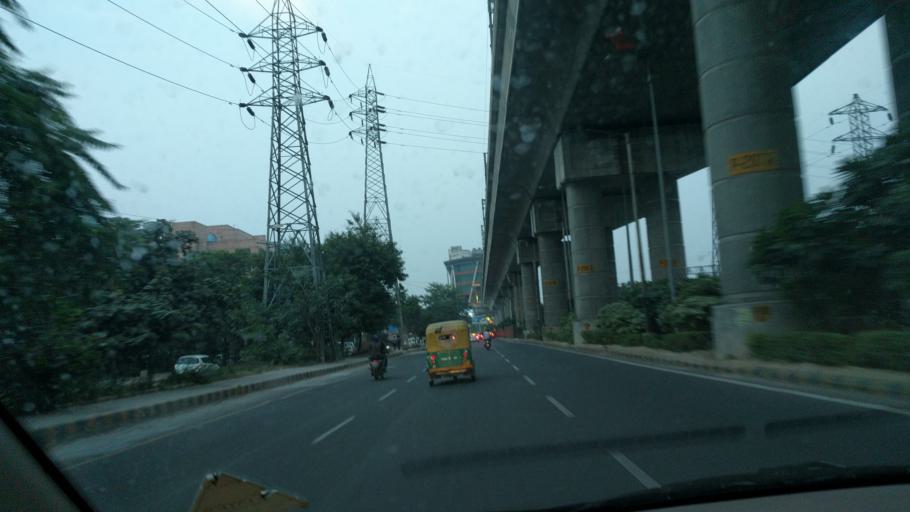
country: IN
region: Haryana
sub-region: Gurgaon
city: Gurgaon
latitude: 28.4565
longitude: 77.0701
